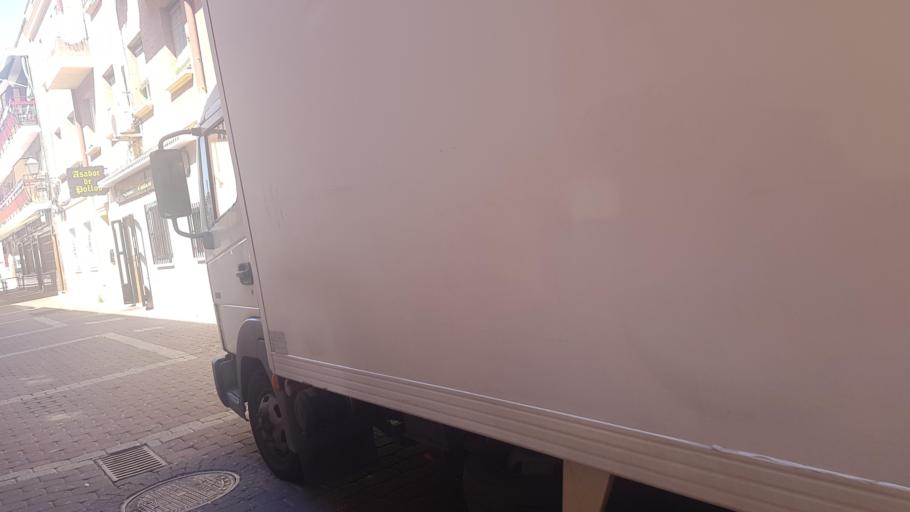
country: ES
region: Madrid
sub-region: Provincia de Madrid
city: Villa de Vallecas
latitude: 40.3798
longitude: -3.6224
